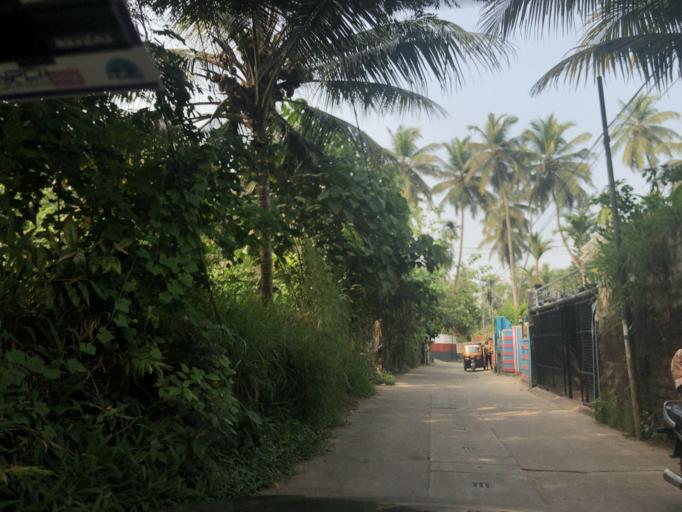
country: IN
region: Kerala
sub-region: Kozhikode
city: Kozhikode
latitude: 11.2789
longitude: 75.7782
